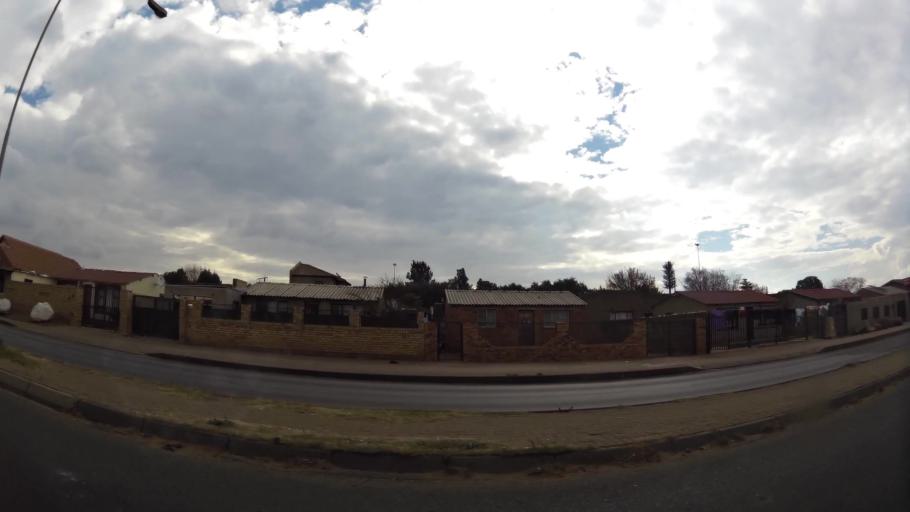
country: ZA
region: Gauteng
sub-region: City of Johannesburg Metropolitan Municipality
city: Soweto
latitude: -26.2381
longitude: 27.8597
